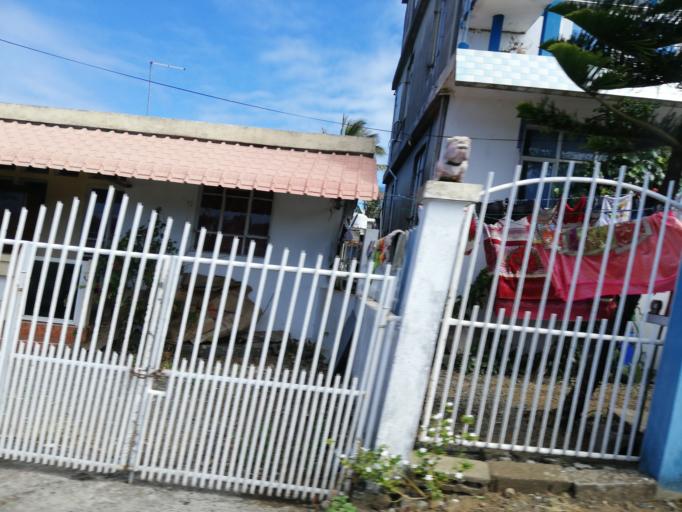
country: MU
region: Grand Port
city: Plaine Magnien
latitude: -20.4590
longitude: 57.6781
